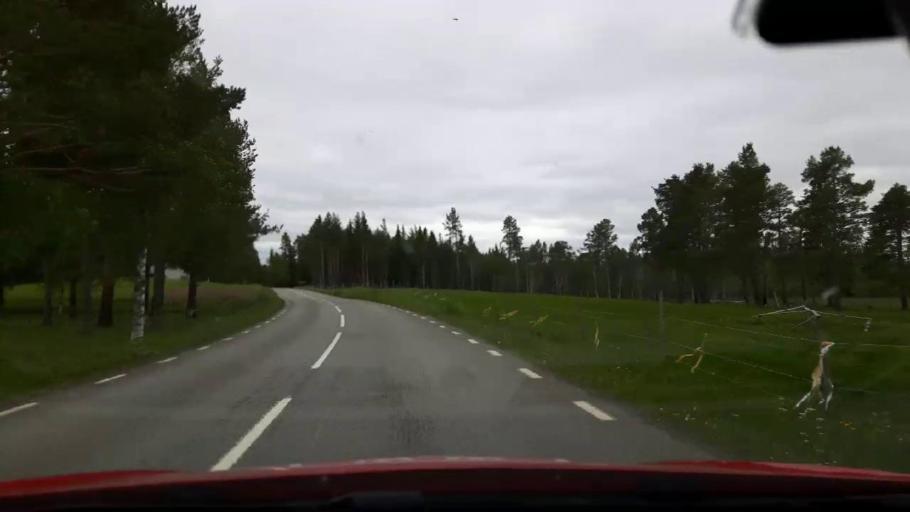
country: SE
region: Jaemtland
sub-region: Stroemsunds Kommun
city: Stroemsund
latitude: 63.4878
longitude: 15.4472
